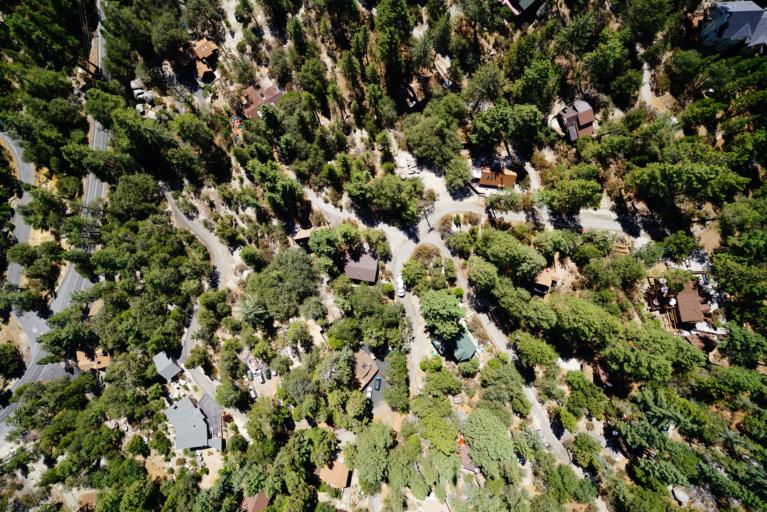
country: US
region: California
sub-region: Riverside County
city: Idyllwild-Pine Cove
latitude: 33.7540
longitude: -116.7263
